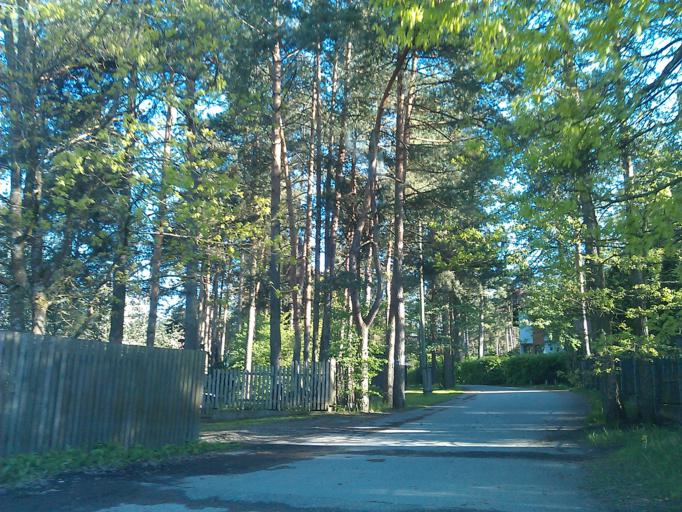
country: LV
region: Riga
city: Bergi
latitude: 57.0163
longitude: 24.2722
